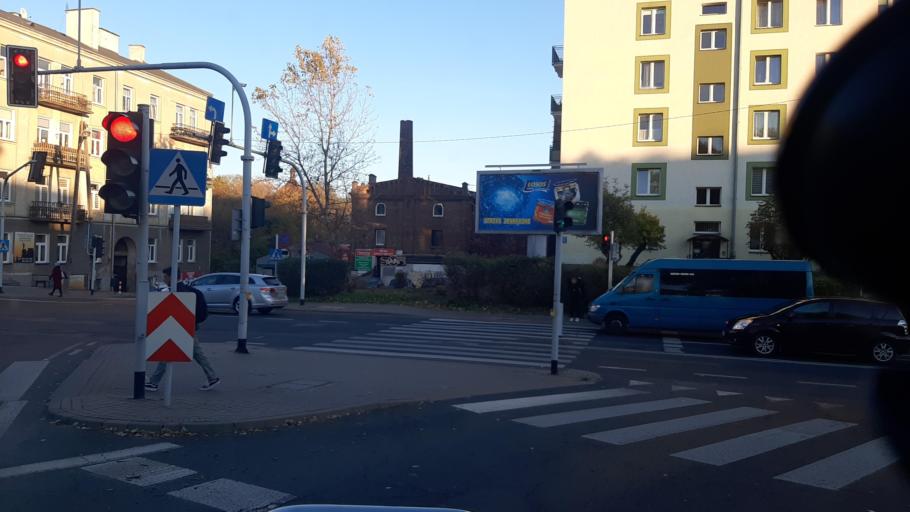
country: PL
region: Lublin Voivodeship
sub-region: Powiat lubelski
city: Lublin
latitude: 51.2555
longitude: 22.5635
